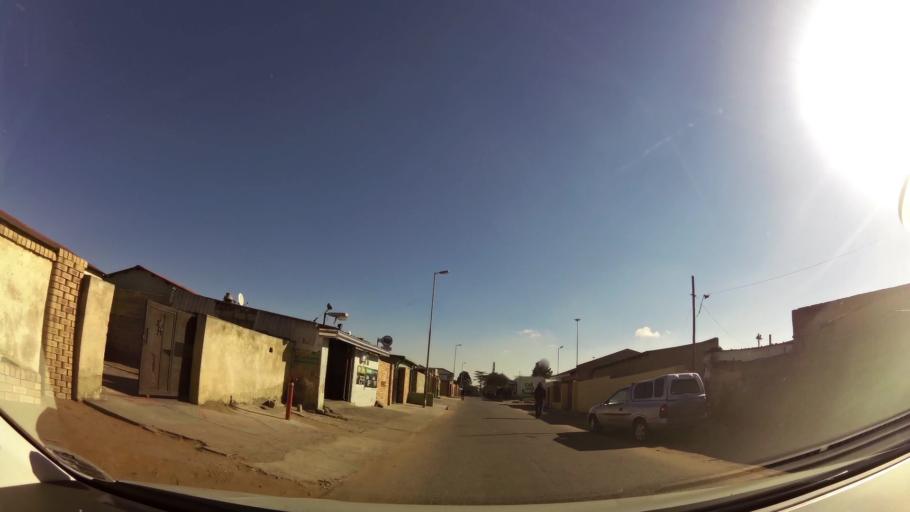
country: ZA
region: Gauteng
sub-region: City of Johannesburg Metropolitan Municipality
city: Roodepoort
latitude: -26.2208
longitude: 27.9167
